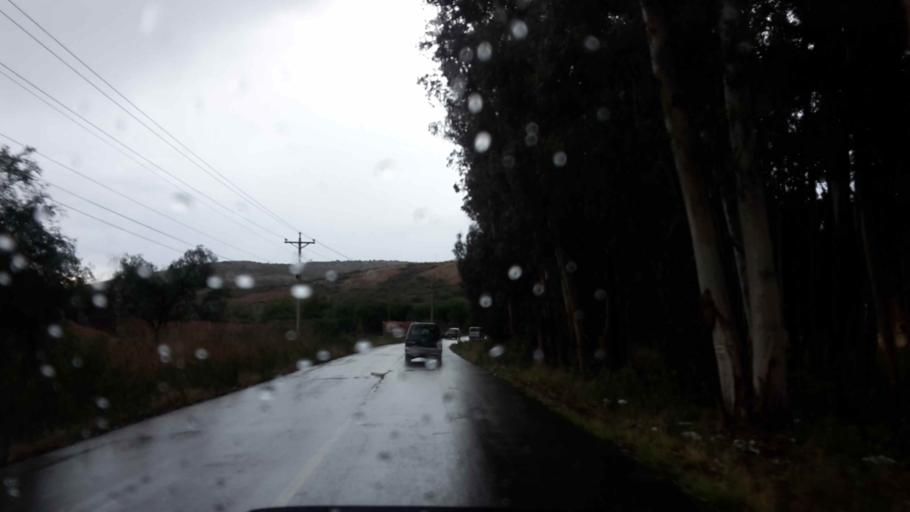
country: BO
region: Cochabamba
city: Tarata
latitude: -17.5401
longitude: -66.1150
